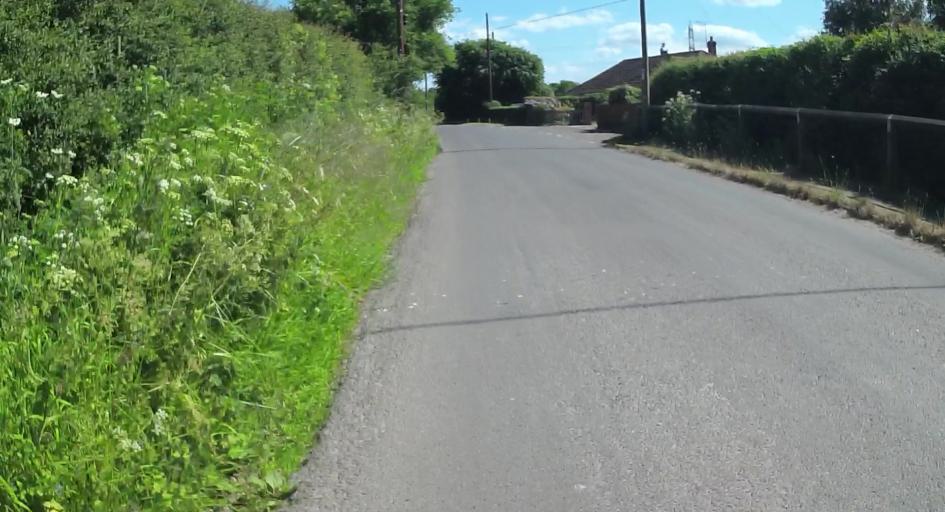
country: GB
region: England
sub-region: Hampshire
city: Hook
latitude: 51.3153
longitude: -0.9998
